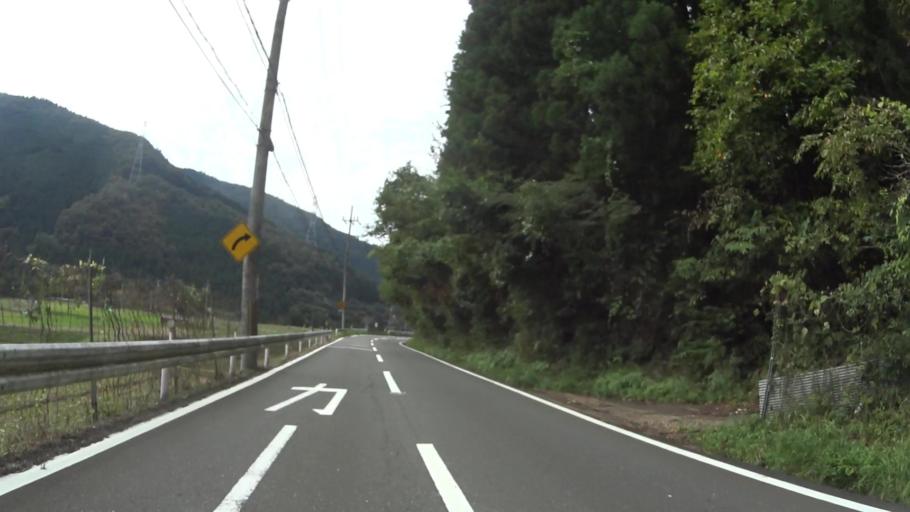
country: JP
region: Kyoto
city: Ayabe
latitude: 35.2593
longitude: 135.4553
